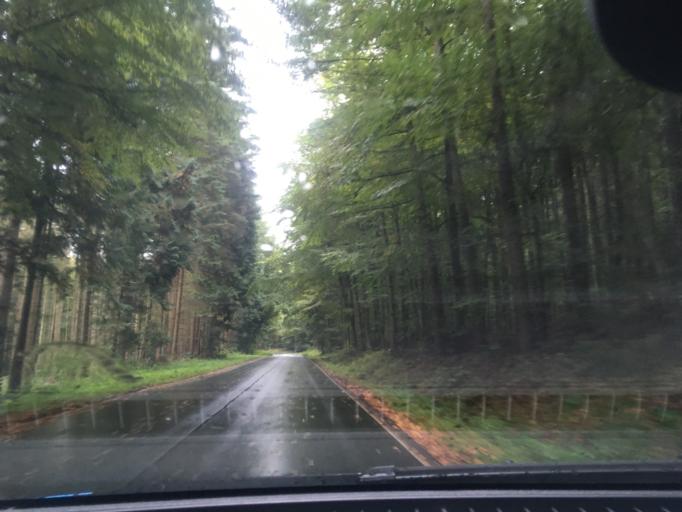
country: DE
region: Lower Saxony
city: Bodenfelde
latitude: 51.6151
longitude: 9.5795
